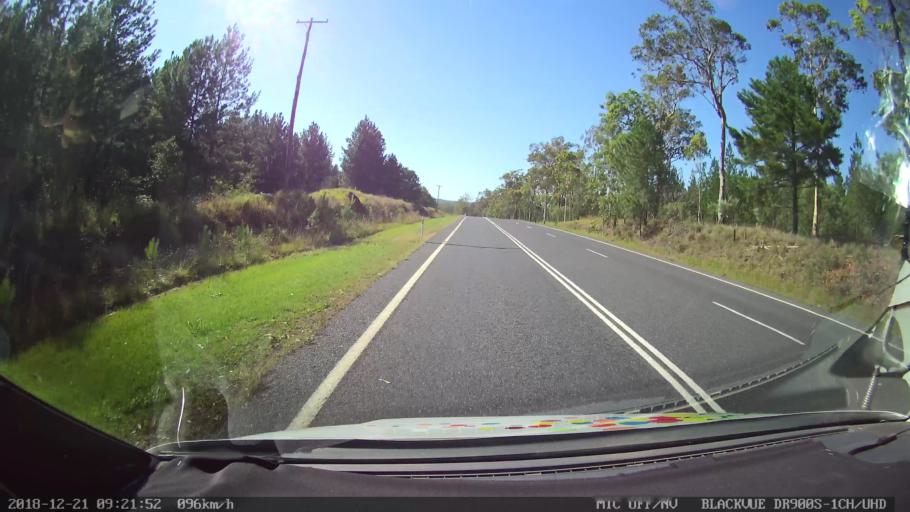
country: AU
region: New South Wales
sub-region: Clarence Valley
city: Maclean
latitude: -29.3347
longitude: 153.0007
